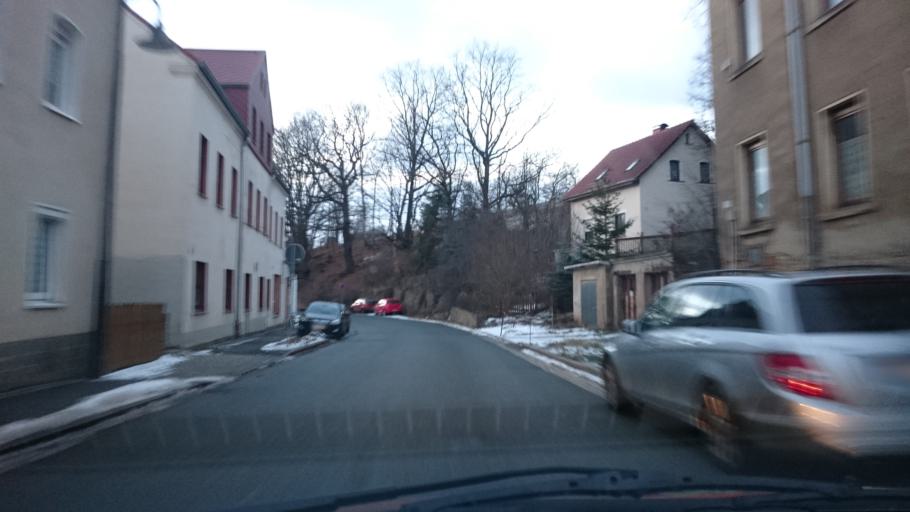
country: DE
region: Saxony
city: Wilkau-Hasslau
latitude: 50.7052
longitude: 12.5400
